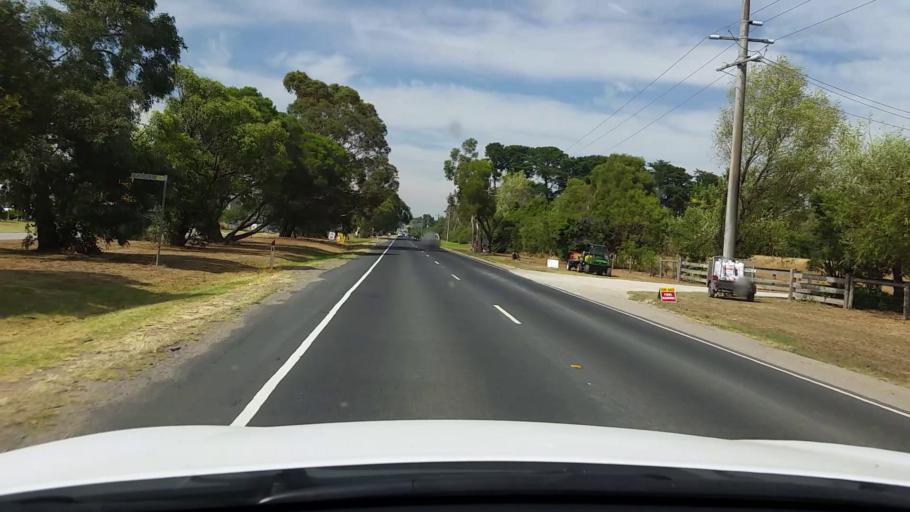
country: AU
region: Victoria
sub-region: Mornington Peninsula
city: Hastings
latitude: -38.2909
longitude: 145.1836
